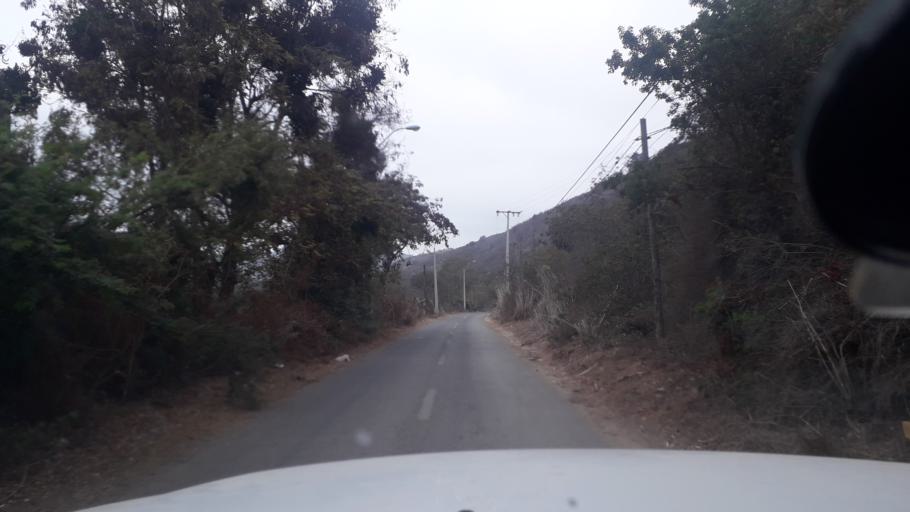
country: CL
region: Valparaiso
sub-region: Provincia de Valparaiso
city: Valparaiso
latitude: -33.1083
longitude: -71.6632
